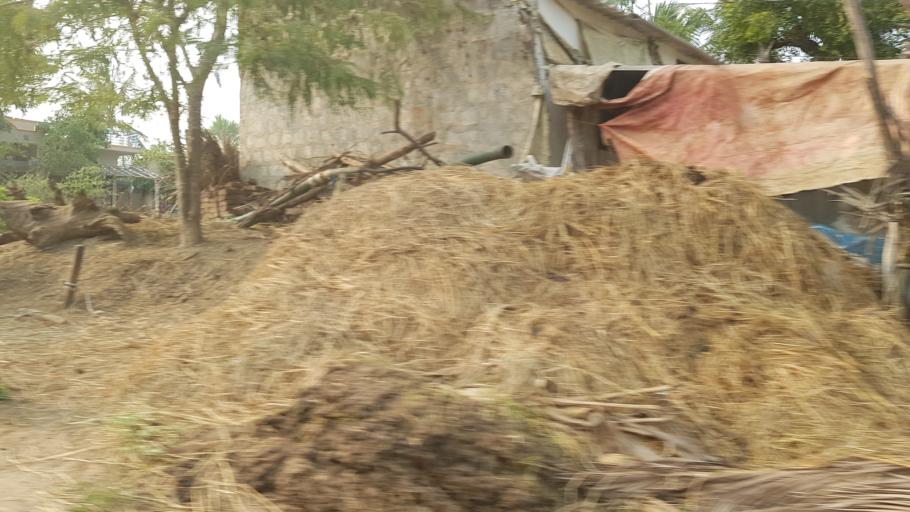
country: IN
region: Andhra Pradesh
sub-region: West Godavari
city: Akividu
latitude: 16.5305
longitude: 81.3899
